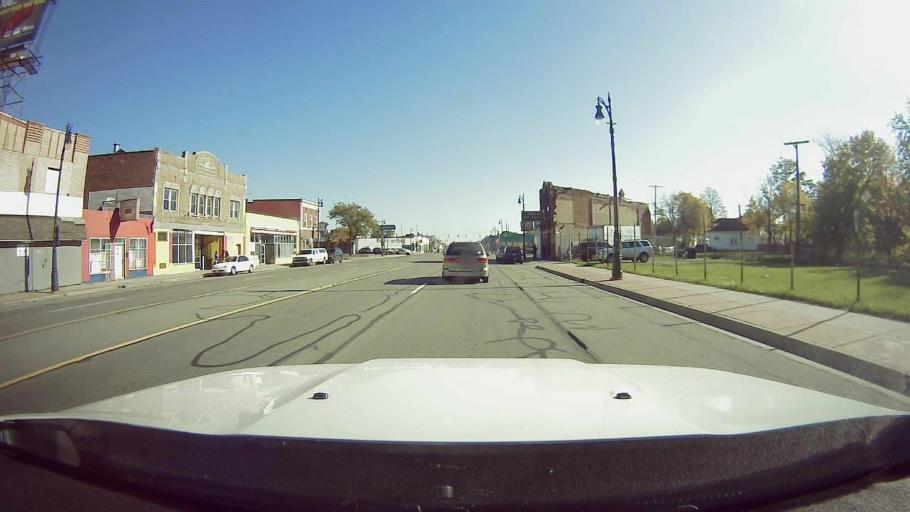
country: US
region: Michigan
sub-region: Wayne County
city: Dearborn
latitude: 42.3310
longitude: -83.1380
